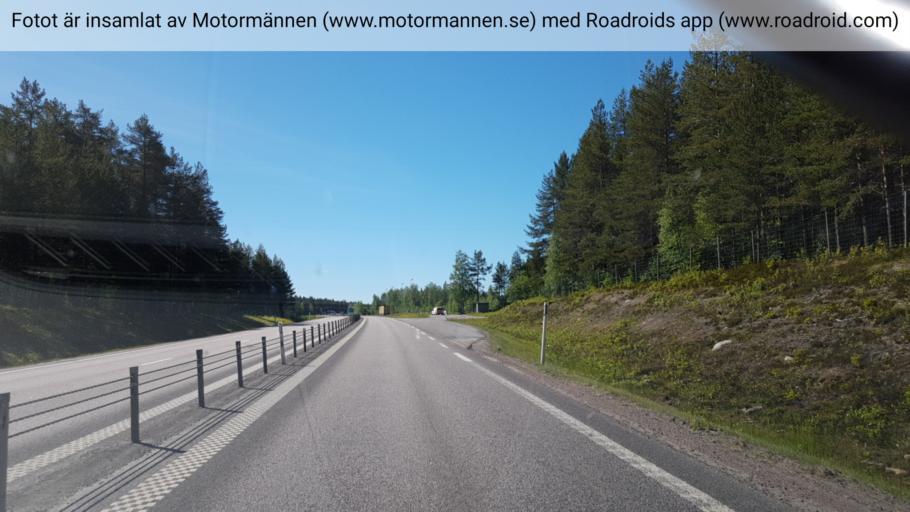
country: SE
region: Norrbotten
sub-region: Pitea Kommun
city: Rosvik
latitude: 65.5150
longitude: 21.7753
